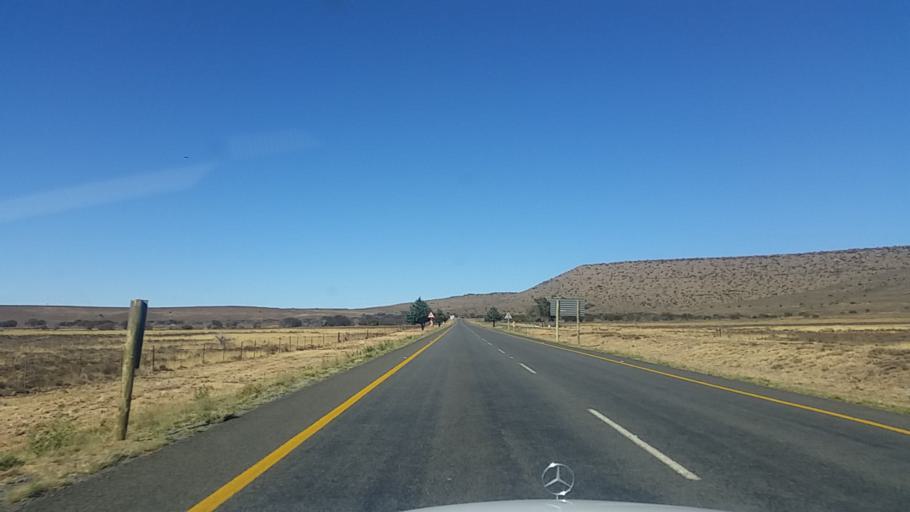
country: ZA
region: Eastern Cape
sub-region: Cacadu District Municipality
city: Graaff-Reinet
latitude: -31.9386
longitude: 24.7351
